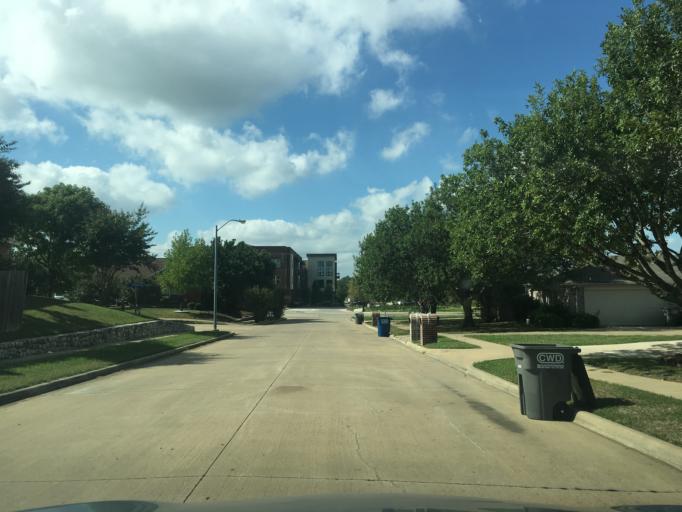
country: US
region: Texas
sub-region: Dallas County
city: Sachse
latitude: 32.9545
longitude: -96.5881
